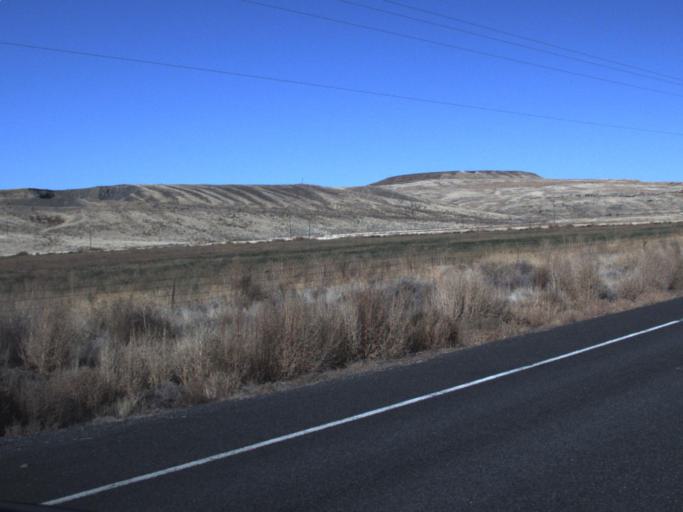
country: US
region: Washington
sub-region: Franklin County
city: Connell
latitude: 46.6738
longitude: -118.4633
